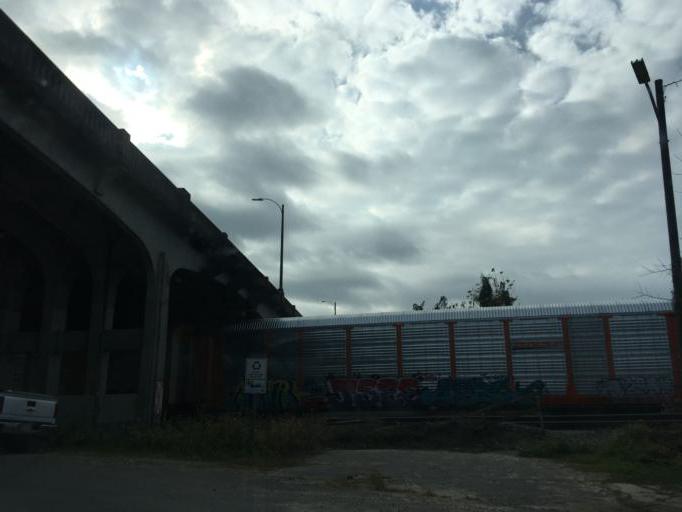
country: US
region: Louisiana
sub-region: Orleans Parish
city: New Orleans
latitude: 29.9860
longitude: -90.0584
